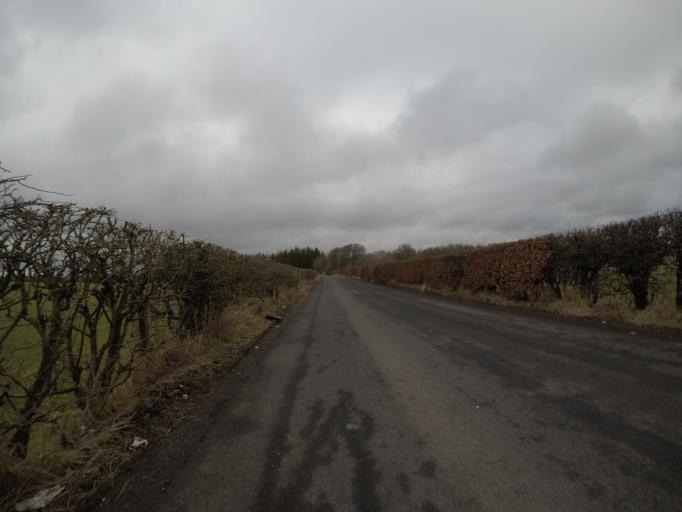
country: GB
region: Scotland
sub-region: North Ayrshire
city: Springside
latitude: 55.6259
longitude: -4.6136
